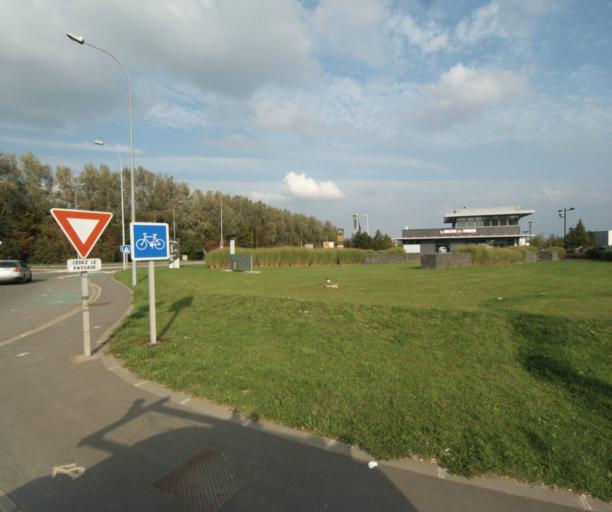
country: FR
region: Nord-Pas-de-Calais
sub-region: Departement du Nord
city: Hallennes-lez-Haubourdin
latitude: 50.6076
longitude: 2.9559
